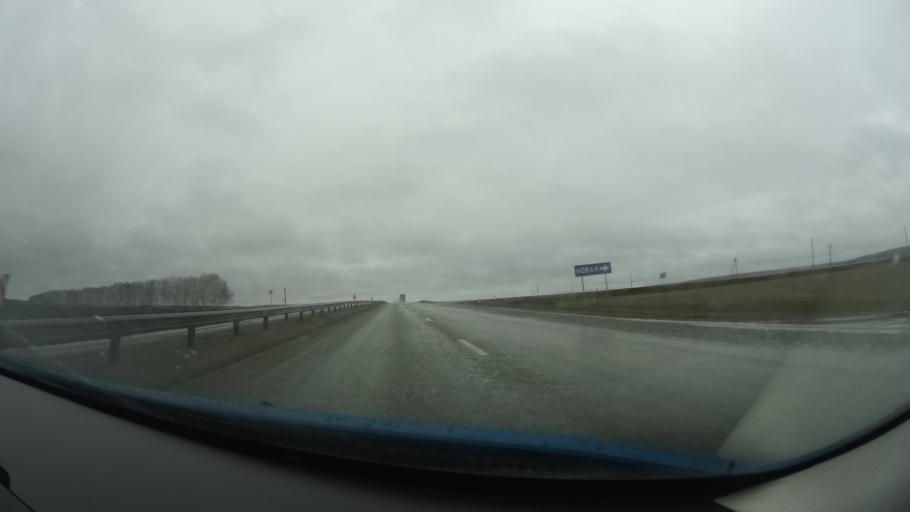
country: RU
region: Bashkortostan
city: Dmitriyevka
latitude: 54.6827
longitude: 55.3261
